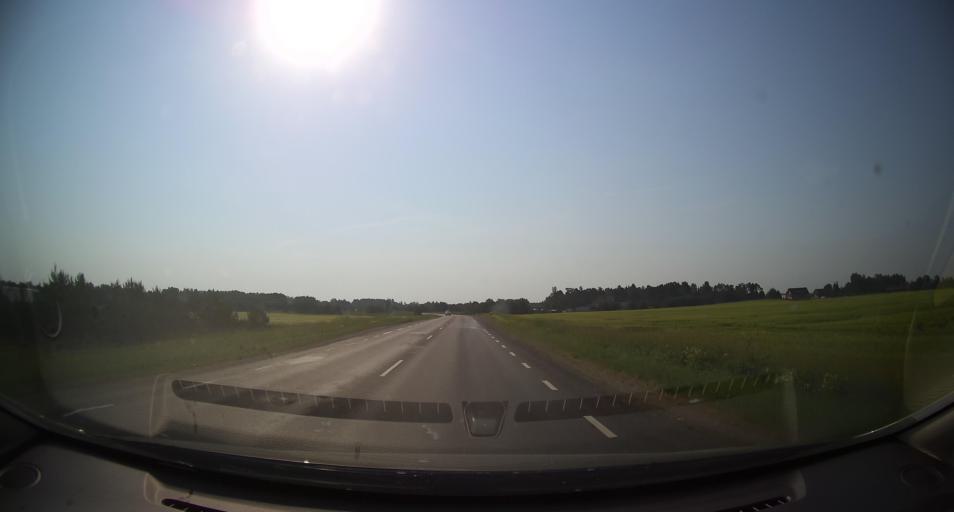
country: EE
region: Harju
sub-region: Raasiku vald
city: Arukula
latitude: 59.3542
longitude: 25.0831
